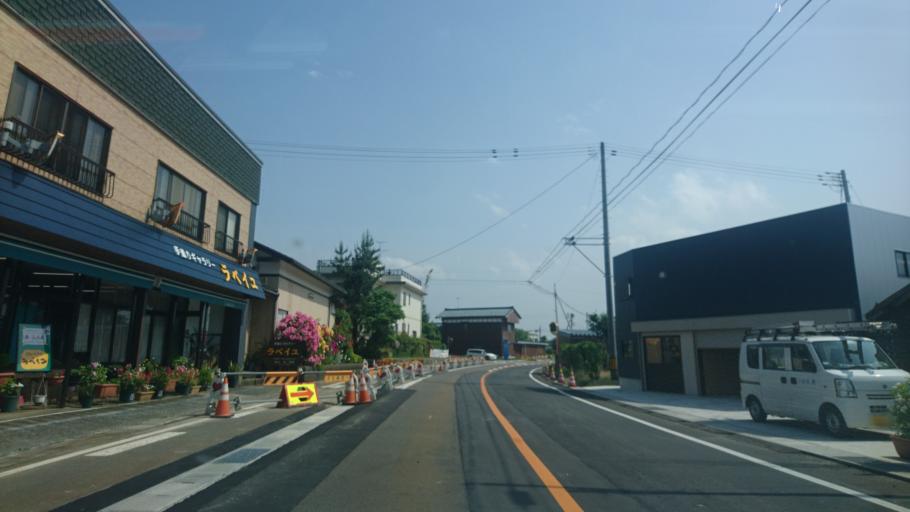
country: JP
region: Niigata
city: Shibata
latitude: 37.9843
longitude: 139.2926
